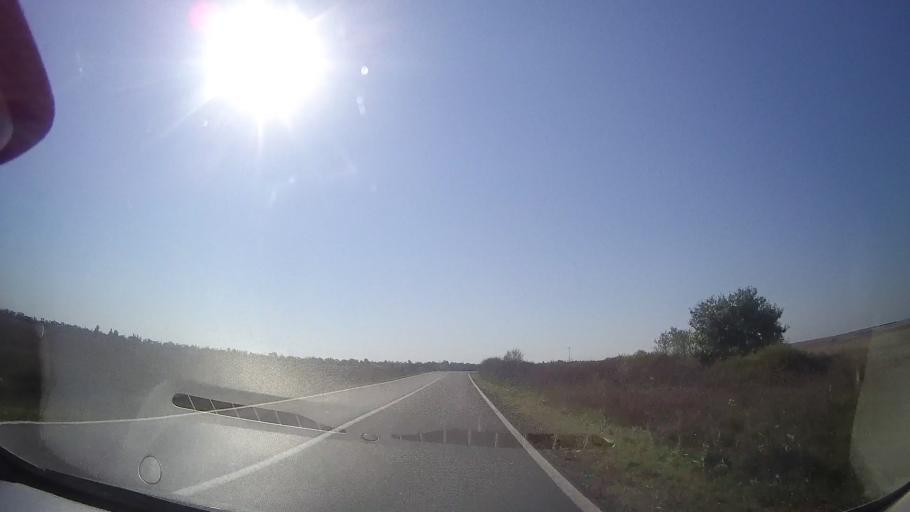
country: RO
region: Timis
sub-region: Comuna Belint
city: Belint
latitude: 45.7773
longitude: 21.7314
